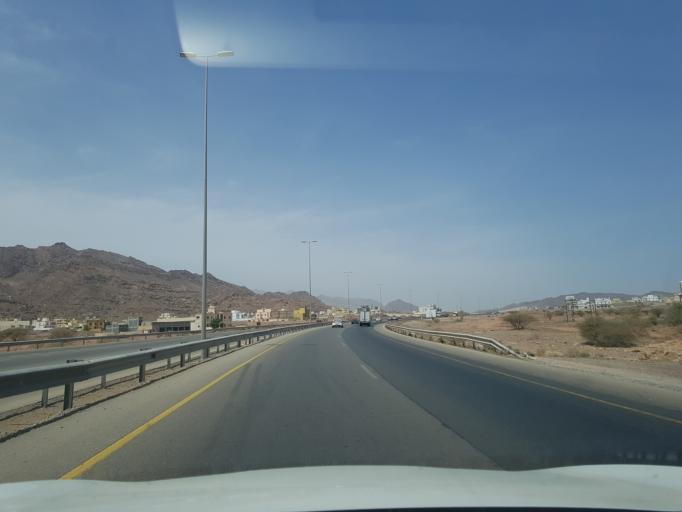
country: OM
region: Muhafazat ad Dakhiliyah
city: Bidbid
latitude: 23.4585
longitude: 58.1723
